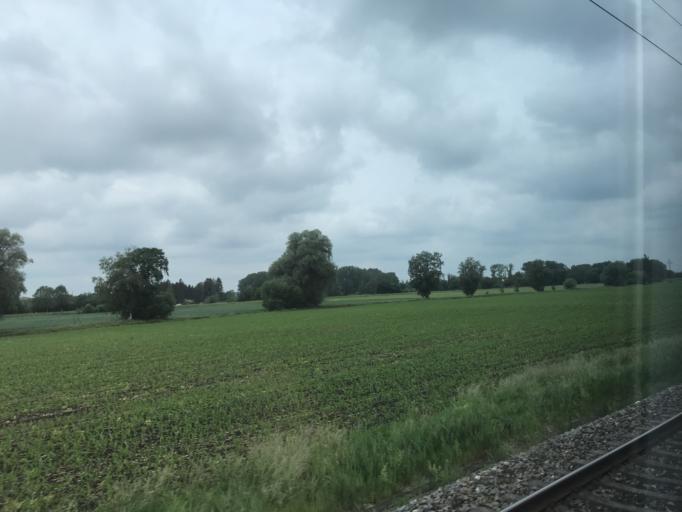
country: DE
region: Bavaria
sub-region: Swabia
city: Burgau
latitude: 48.4473
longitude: 10.4134
